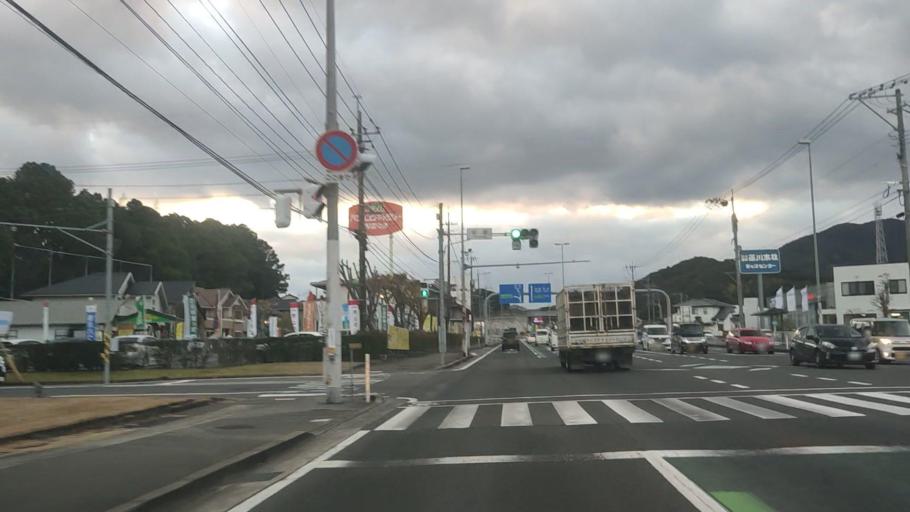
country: JP
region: Nagasaki
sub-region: Isahaya-shi
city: Isahaya
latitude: 32.8189
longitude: 129.9692
